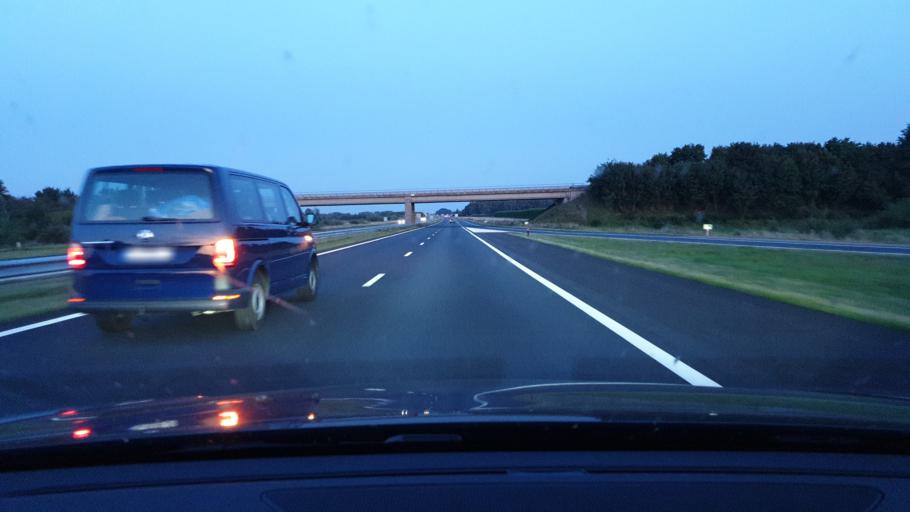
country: NL
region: North Brabant
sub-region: Gemeente Moerdijk
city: Willemstad
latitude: 51.6581
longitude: 4.4239
